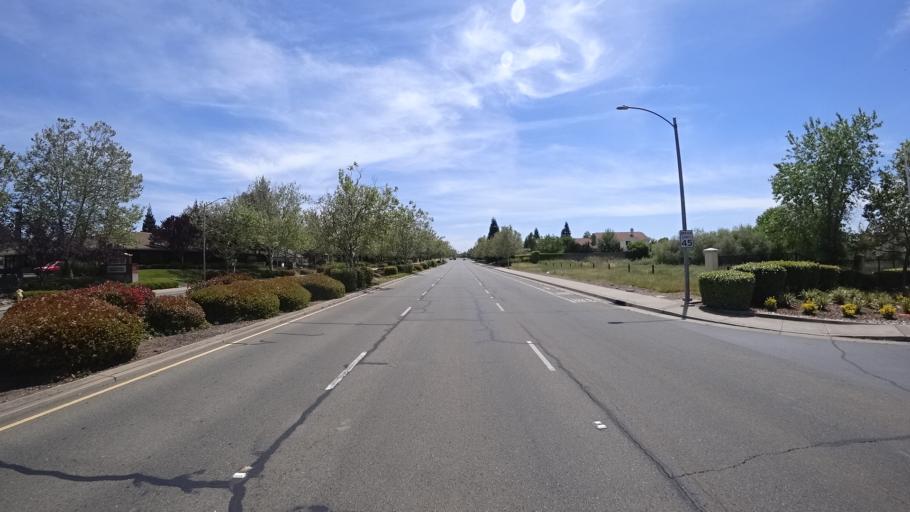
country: US
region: California
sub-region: Placer County
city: Rocklin
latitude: 38.8035
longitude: -121.2719
